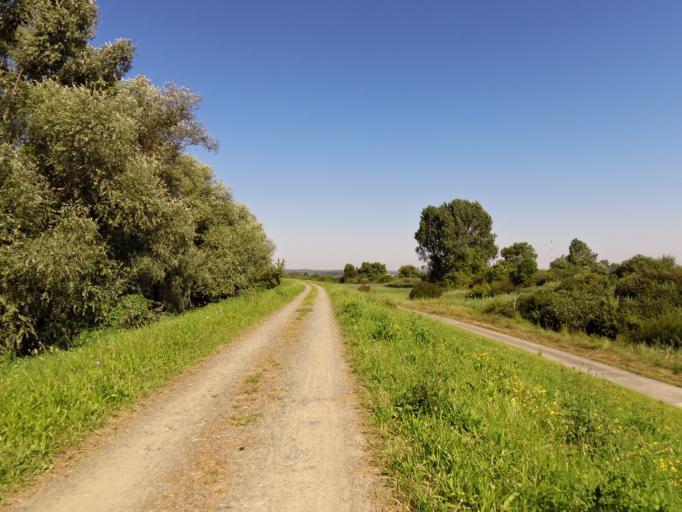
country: DE
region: Rheinland-Pfalz
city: Oppenheim
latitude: 49.8578
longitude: 8.3872
